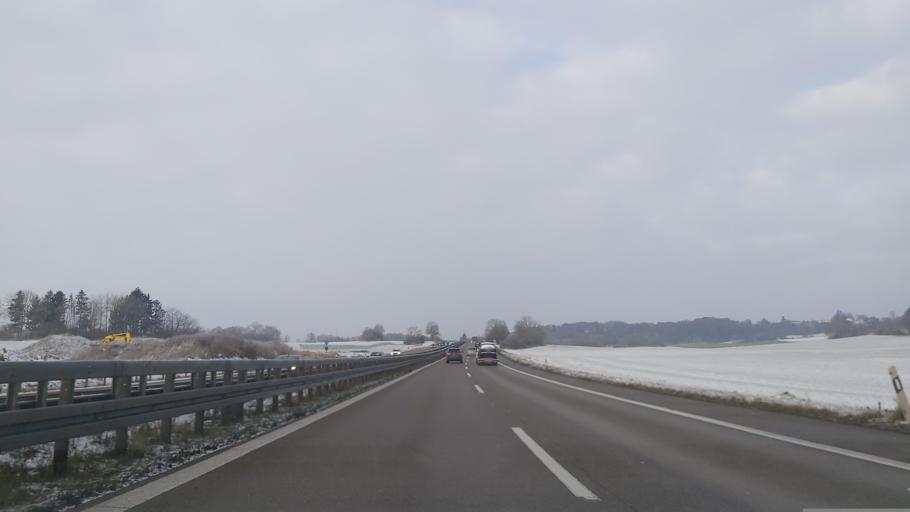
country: DE
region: Baden-Wuerttemberg
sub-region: Regierungsbezirk Stuttgart
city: Hohenstadt
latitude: 48.5302
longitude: 9.6783
